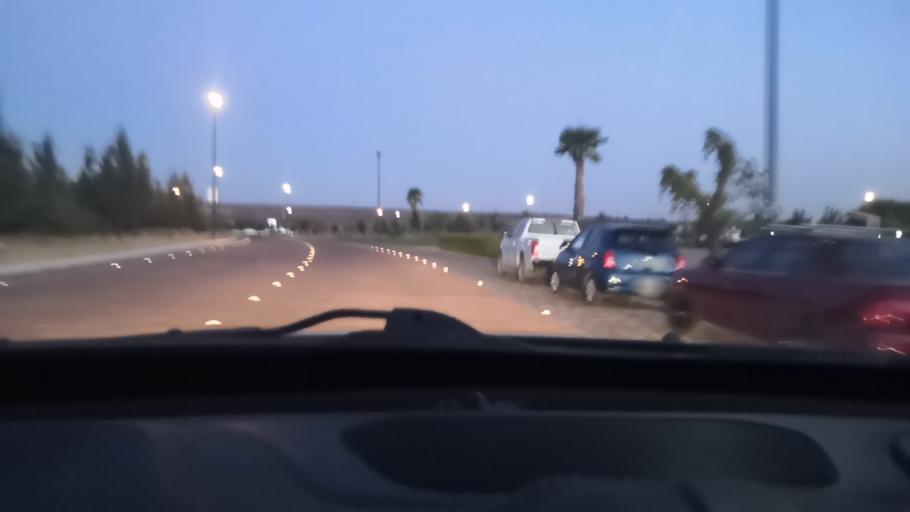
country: MX
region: Guanajuato
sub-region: Leon
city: Fraccionamiento Paseo de las Torres
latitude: 21.2330
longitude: -101.7948
